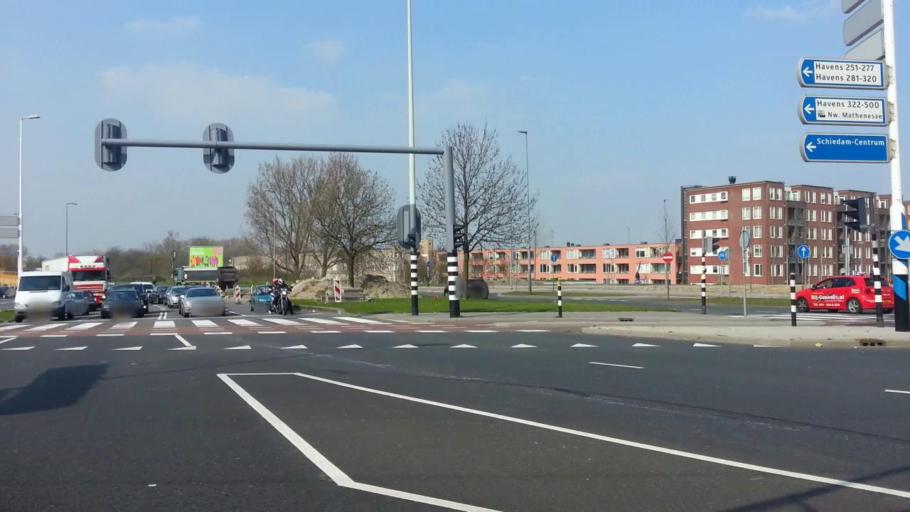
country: NL
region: South Holland
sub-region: Gemeente Rotterdam
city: Delfshaven
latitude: 51.9133
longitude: 4.4304
